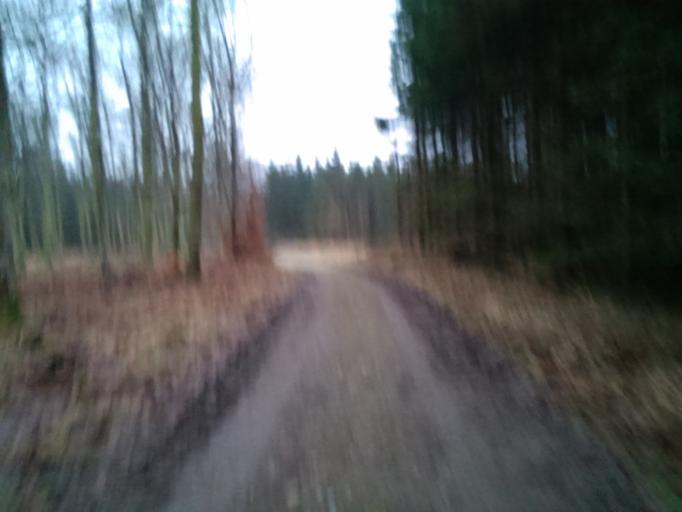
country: DK
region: North Denmark
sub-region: Mariagerfjord Kommune
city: Arden
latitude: 56.7985
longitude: 9.7543
